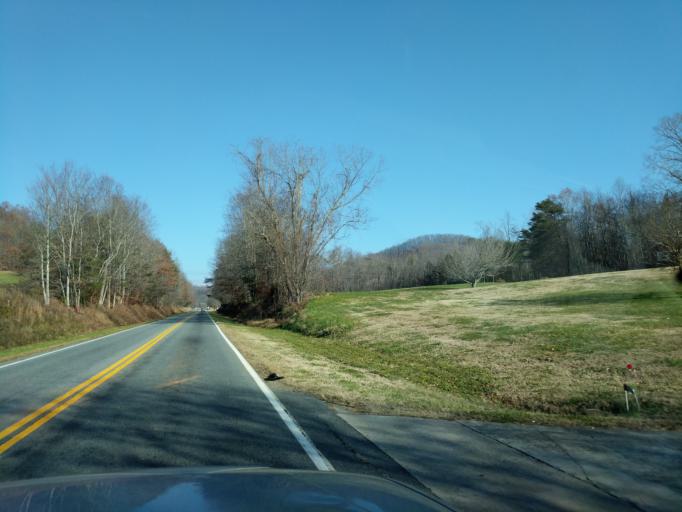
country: US
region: North Carolina
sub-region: McDowell County
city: West Marion
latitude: 35.6299
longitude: -81.9864
